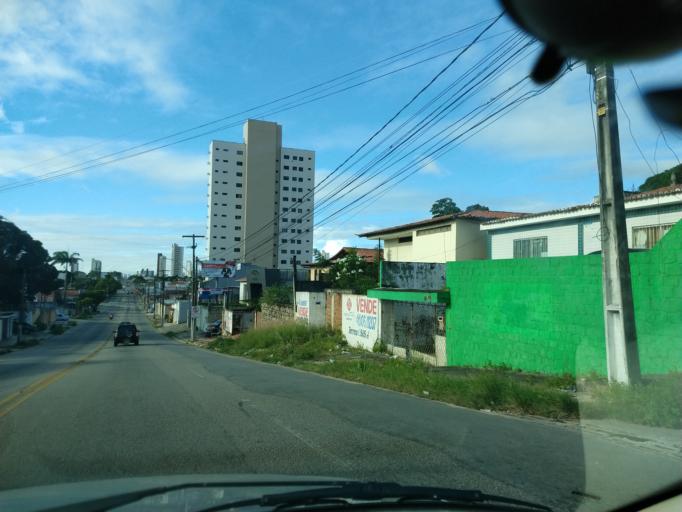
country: BR
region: Rio Grande do Norte
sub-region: Natal
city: Natal
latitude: -5.8278
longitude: -35.2215
